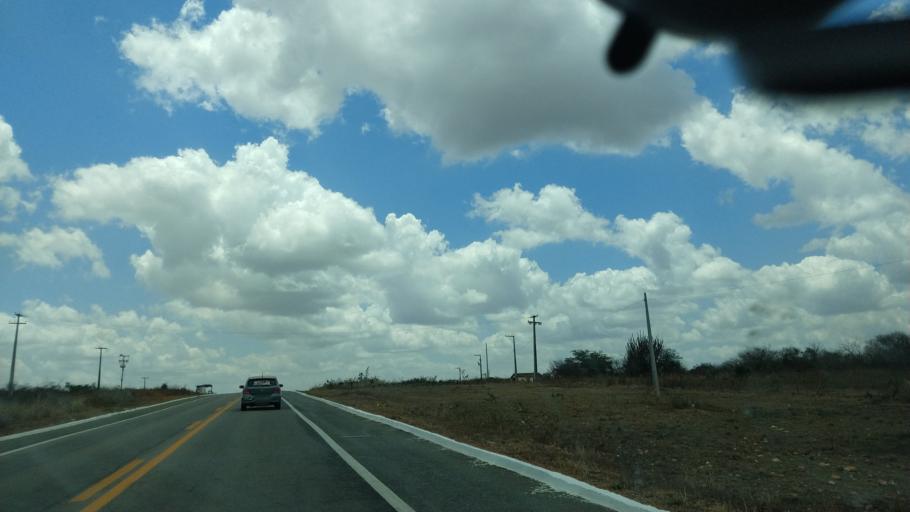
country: BR
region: Rio Grande do Norte
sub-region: Cerro Cora
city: Cerro Cora
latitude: -6.1888
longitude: -36.2320
